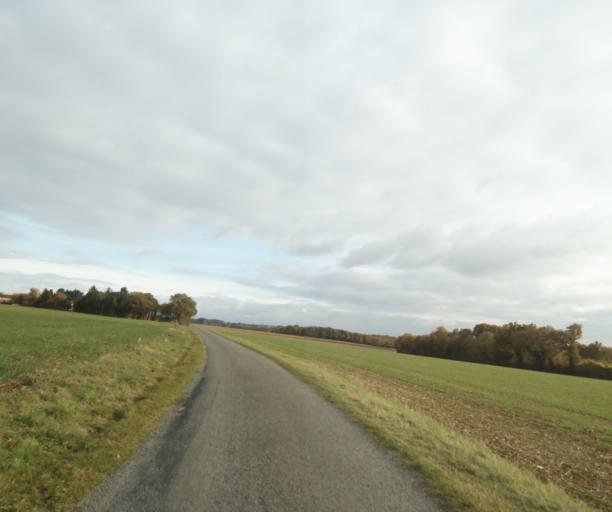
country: FR
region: Poitou-Charentes
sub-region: Departement de la Charente-Maritime
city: Nieul-les-Saintes
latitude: 45.7850
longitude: -0.7366
